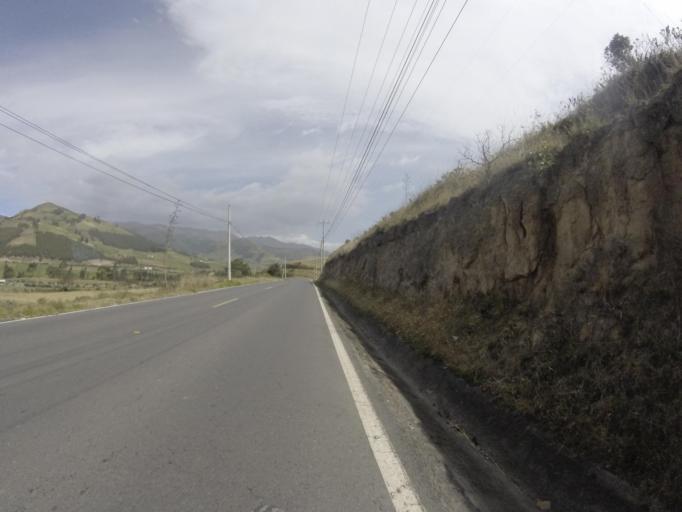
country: EC
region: Pichincha
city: Cayambe
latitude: 0.1252
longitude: -78.0823
